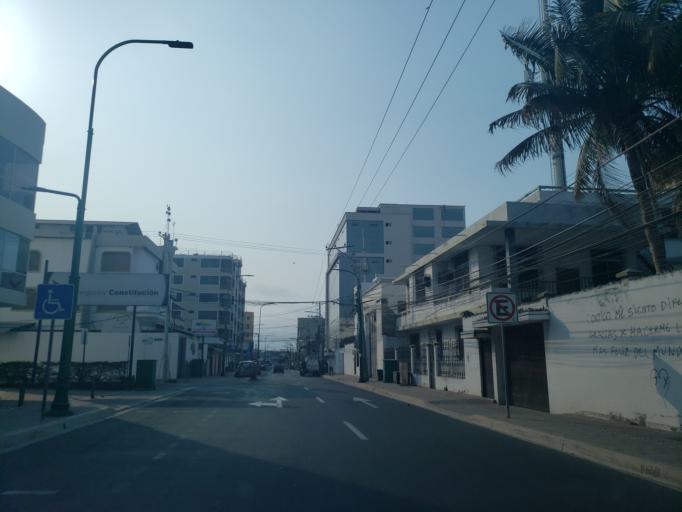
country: EC
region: Manabi
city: Manta
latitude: -0.9448
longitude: -80.7383
